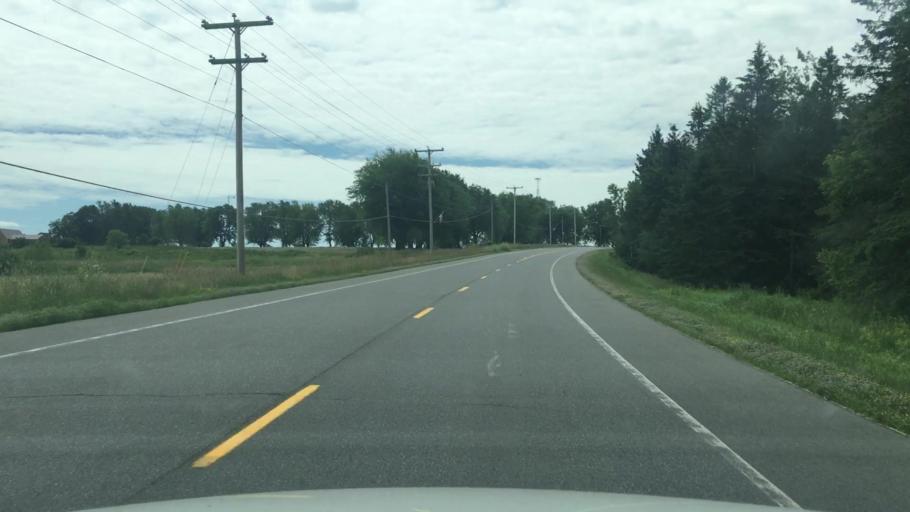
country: US
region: Maine
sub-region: Waldo County
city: Troy
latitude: 44.5446
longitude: -69.2653
